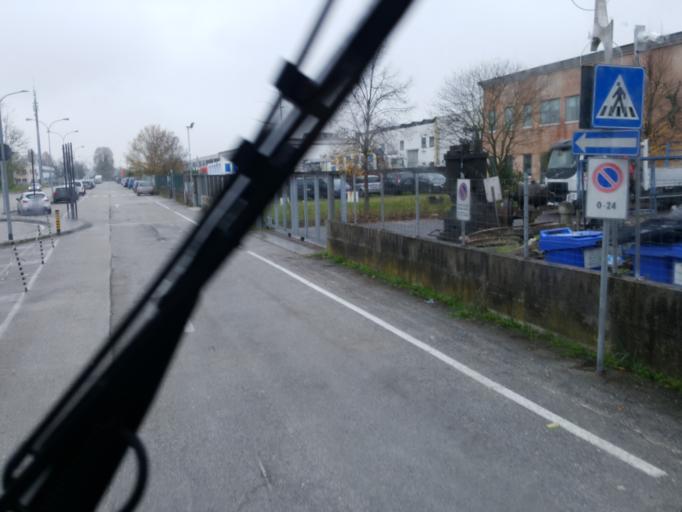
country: IT
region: Veneto
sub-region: Provincia di Treviso
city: Mogliano Veneto
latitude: 45.5546
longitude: 12.2269
